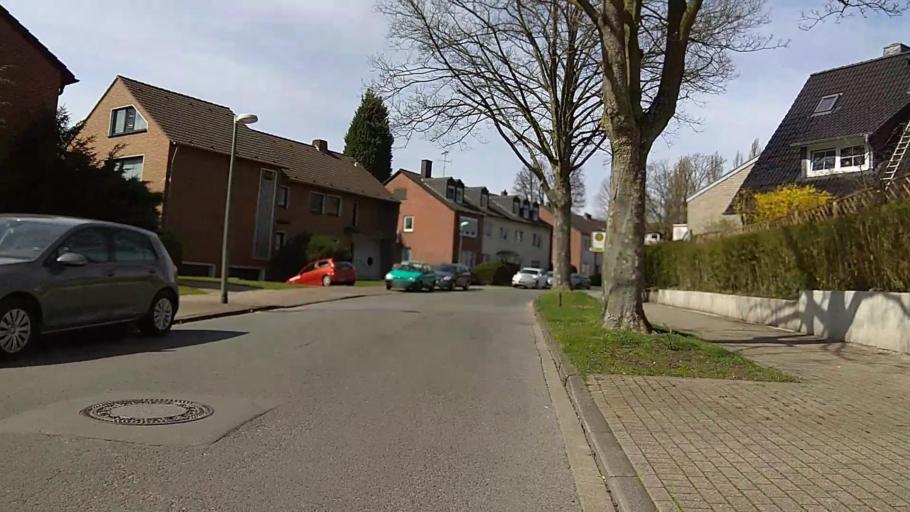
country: DE
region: North Rhine-Westphalia
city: Herten
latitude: 51.5789
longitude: 7.0713
